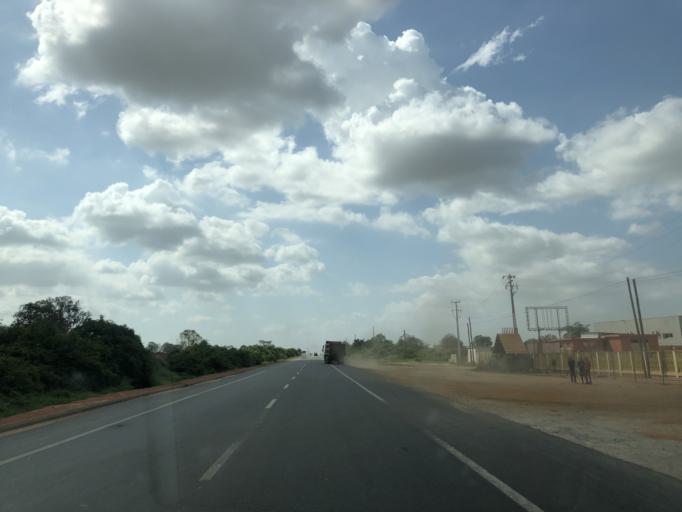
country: AO
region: Luanda
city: Luanda
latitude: -9.0250
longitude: 13.5571
